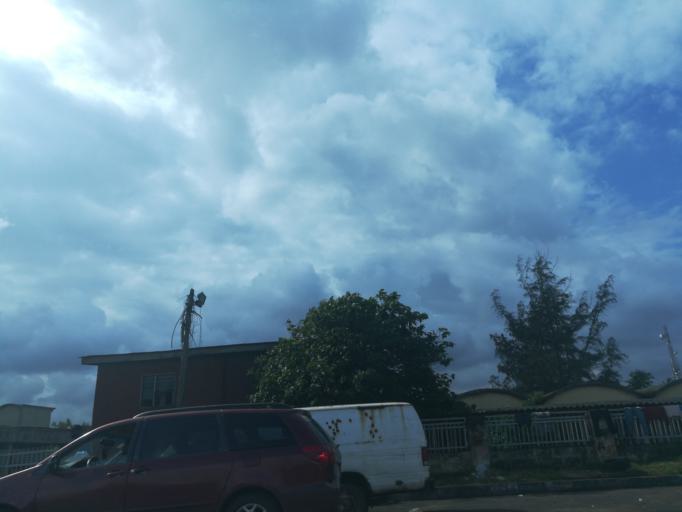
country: NG
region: Lagos
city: Agege
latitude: 6.6198
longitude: 3.3383
